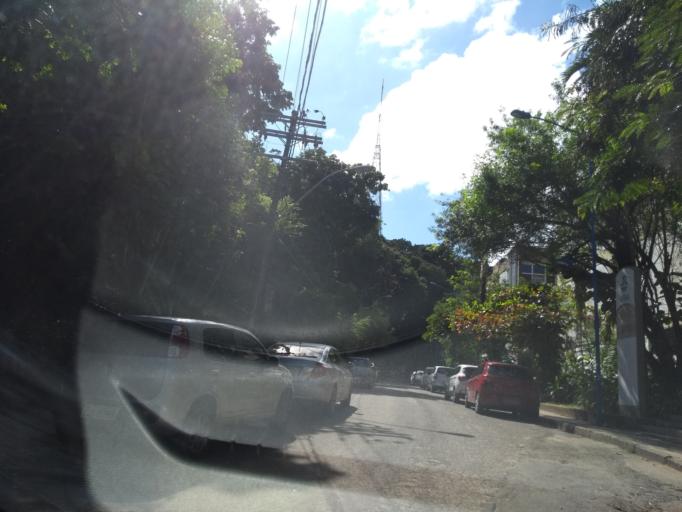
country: BR
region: Bahia
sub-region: Salvador
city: Salvador
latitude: -12.9983
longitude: -38.5074
